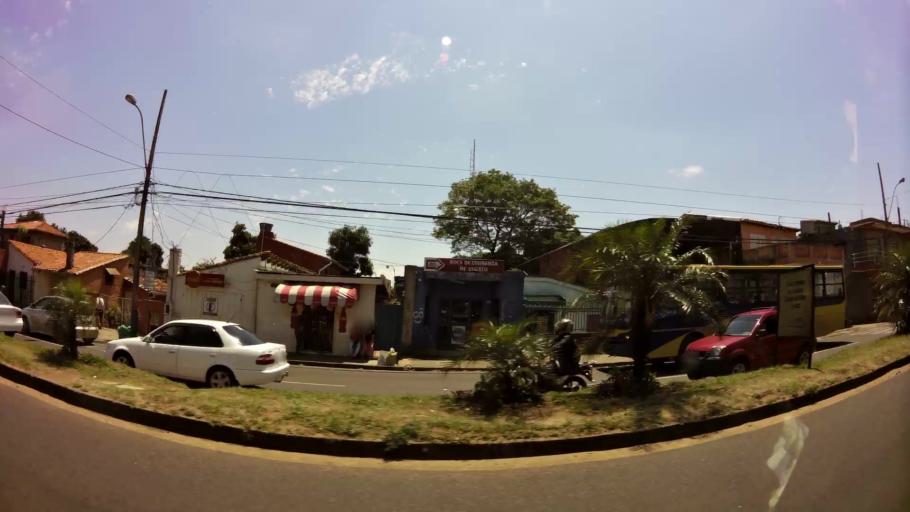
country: PY
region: Central
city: Lambare
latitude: -25.3333
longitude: -57.5773
